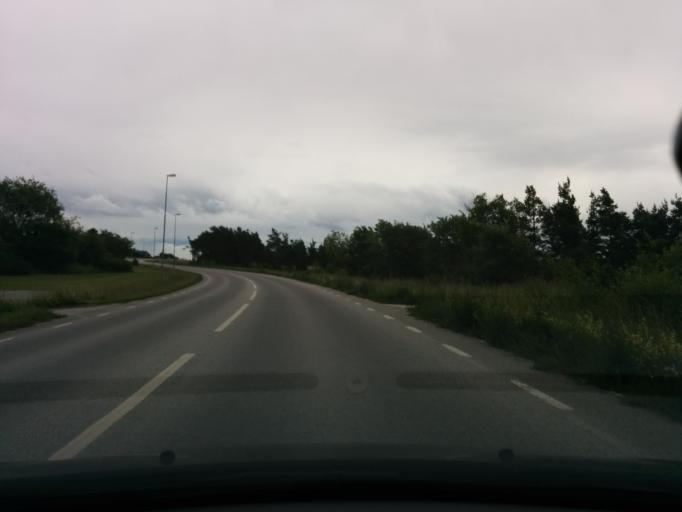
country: SE
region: Gotland
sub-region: Gotland
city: Slite
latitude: 57.6987
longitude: 18.7952
